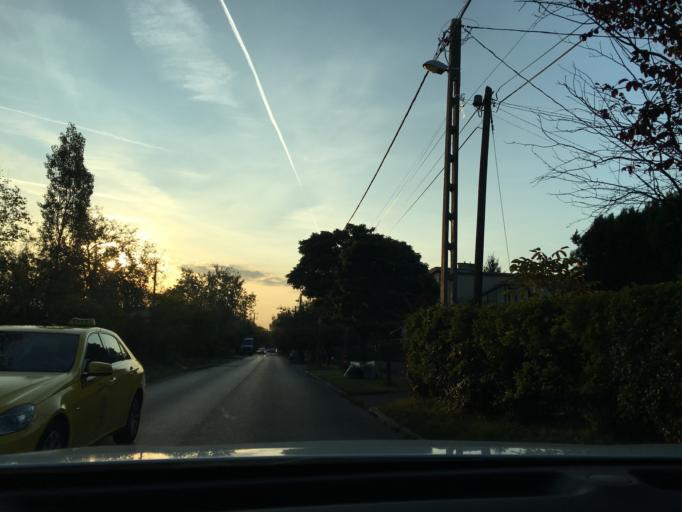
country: HU
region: Budapest
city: Budapest XVII. keruelet
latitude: 47.4755
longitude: 19.2502
